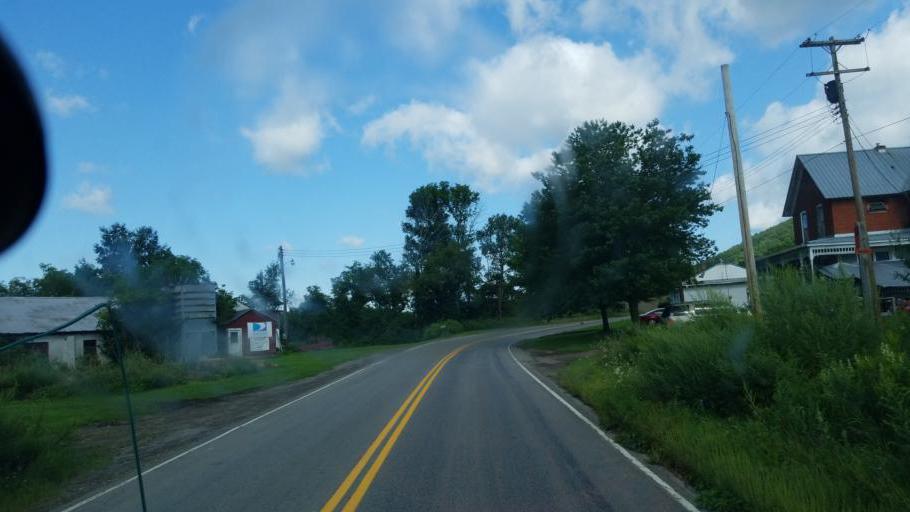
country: US
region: New York
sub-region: Steuben County
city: Canisteo
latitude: 42.2971
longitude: -77.6290
